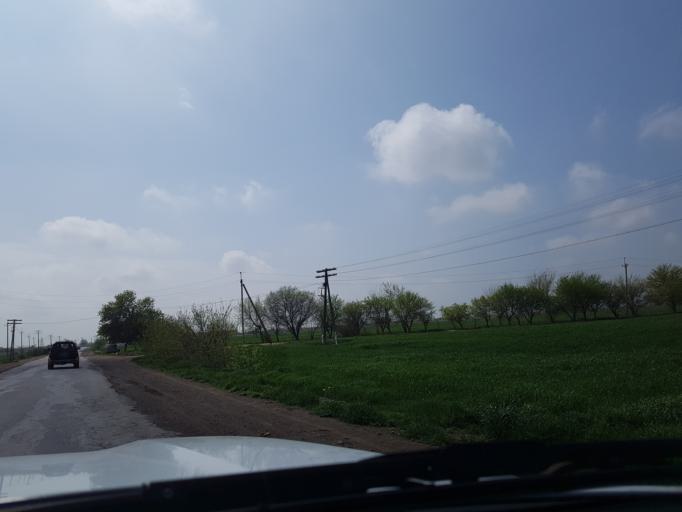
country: TM
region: Lebap
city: Turkmenabat
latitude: 38.9576
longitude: 63.6759
